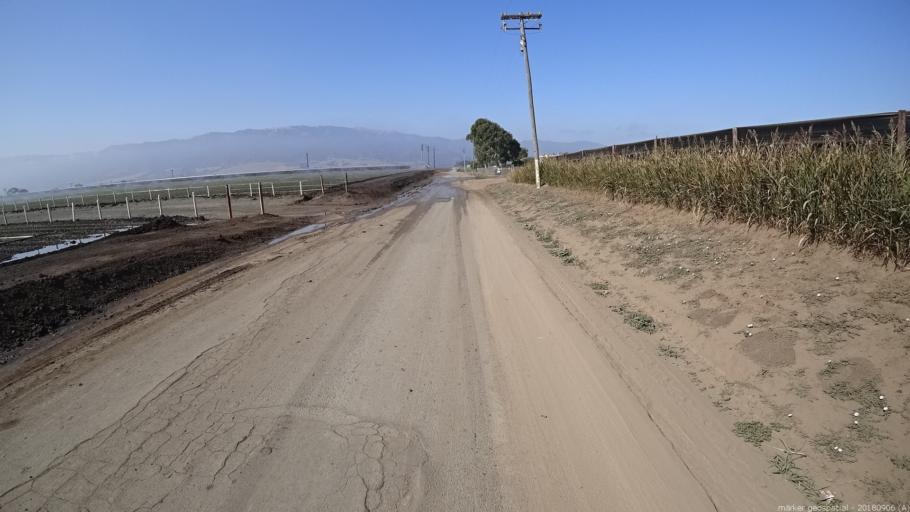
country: US
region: California
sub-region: Monterey County
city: Chualar
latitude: 36.5930
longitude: -121.5517
